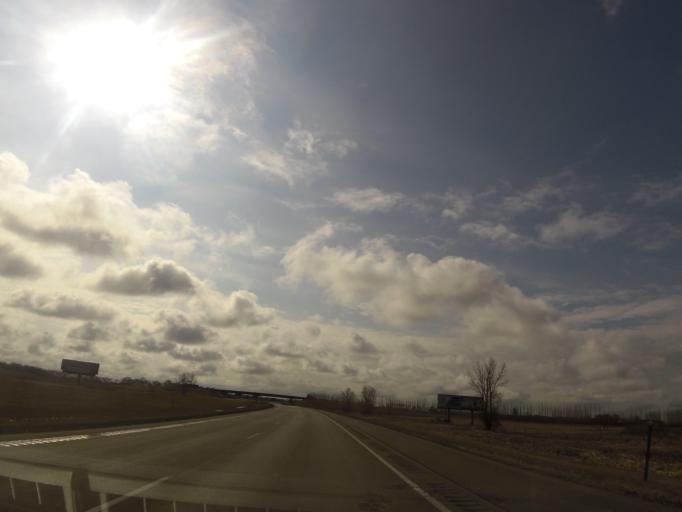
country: US
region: North Dakota
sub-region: Grand Forks County
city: Grand Forks
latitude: 47.8493
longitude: -97.0861
